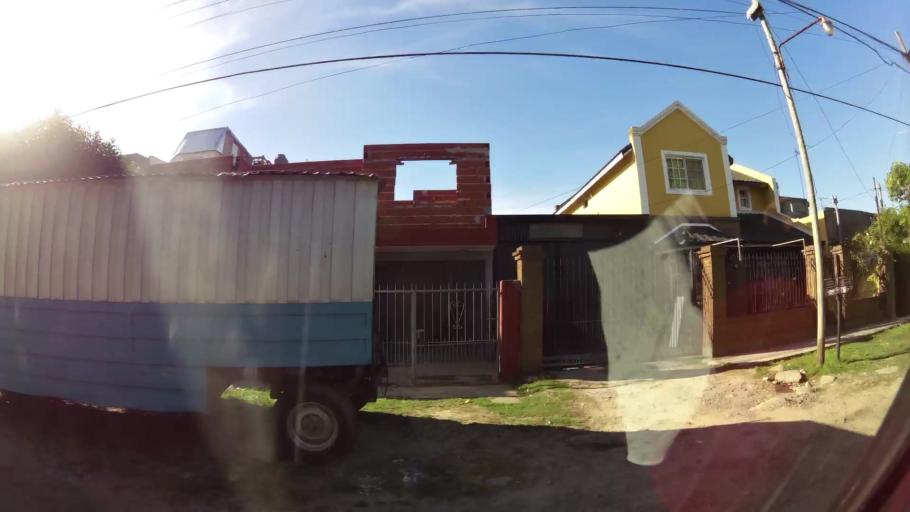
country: AR
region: Buenos Aires
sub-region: Partido de Almirante Brown
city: Adrogue
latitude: -34.8220
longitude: -58.3599
